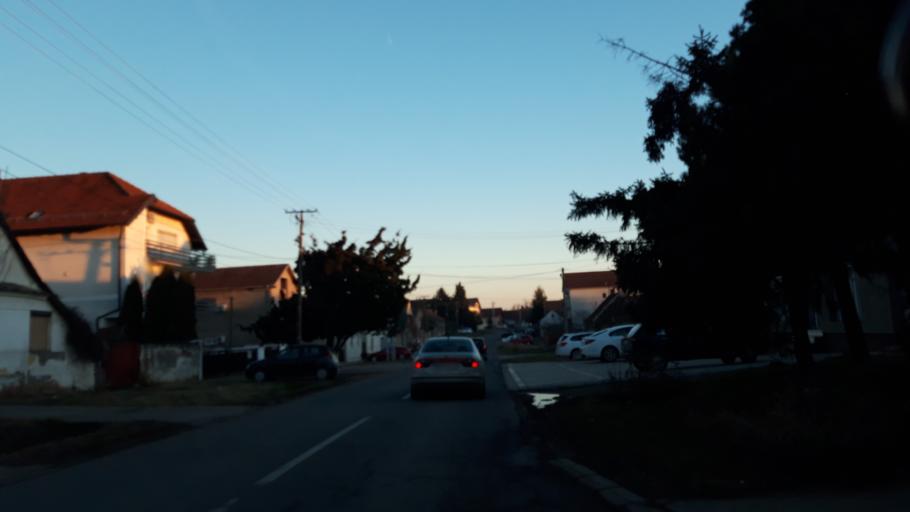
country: RS
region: Autonomna Pokrajina Vojvodina
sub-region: Sremski Okrug
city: Ingija
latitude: 45.0435
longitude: 20.0761
